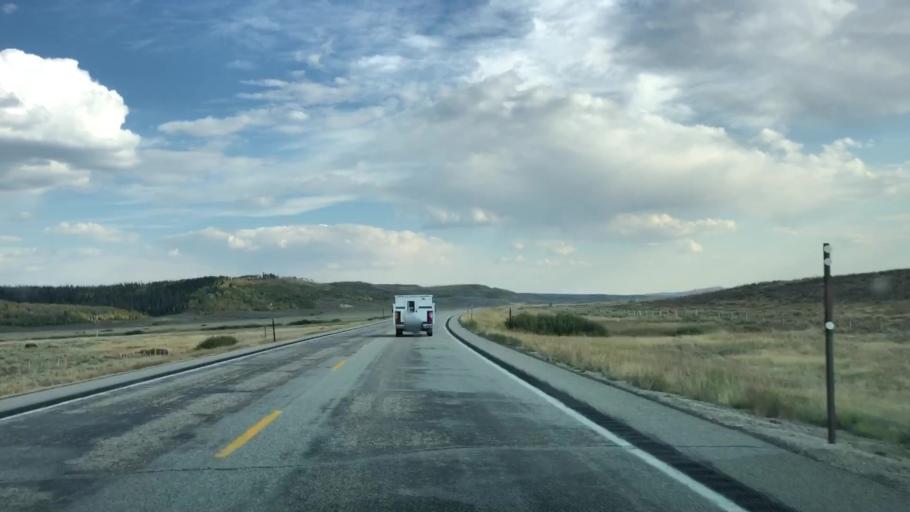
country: US
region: Wyoming
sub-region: Sublette County
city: Pinedale
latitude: 43.1148
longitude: -110.1756
